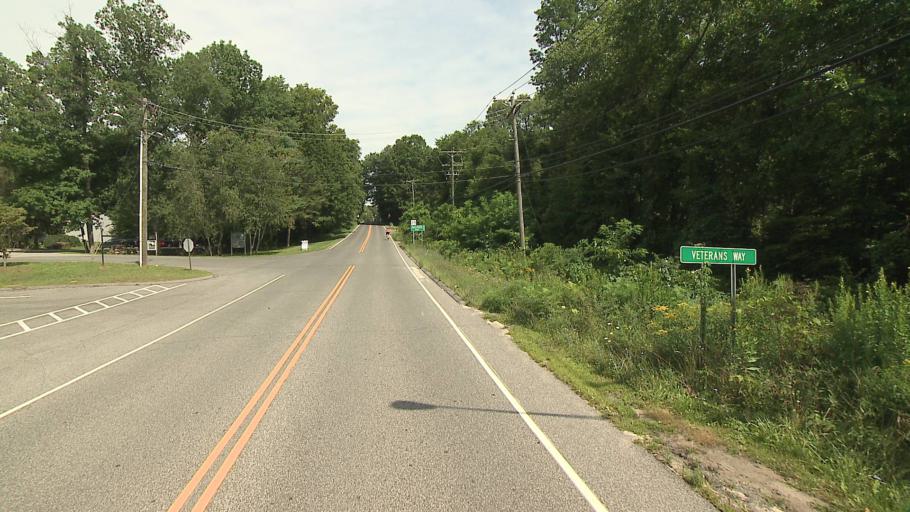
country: US
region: Connecticut
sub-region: Fairfield County
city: Sherman
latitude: 41.5800
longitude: -73.4971
